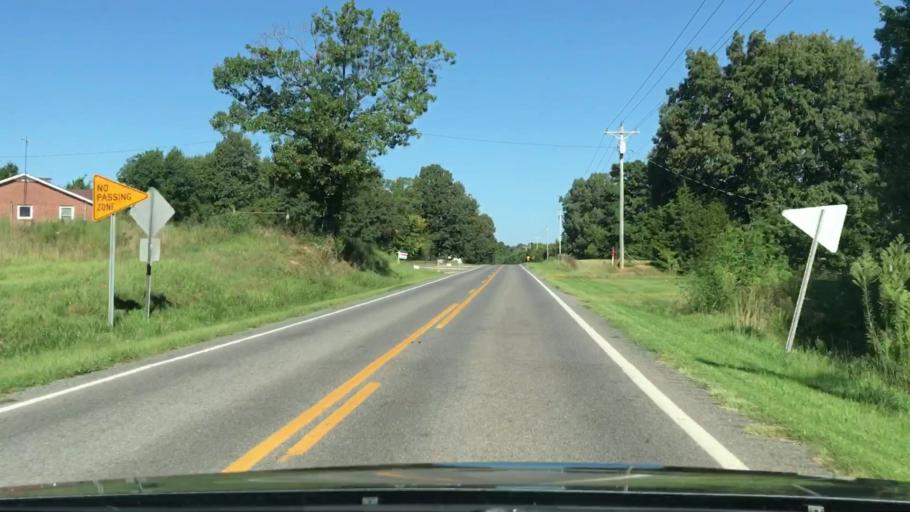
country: US
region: Kentucky
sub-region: Graves County
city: Mayfield
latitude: 36.7760
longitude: -88.5071
